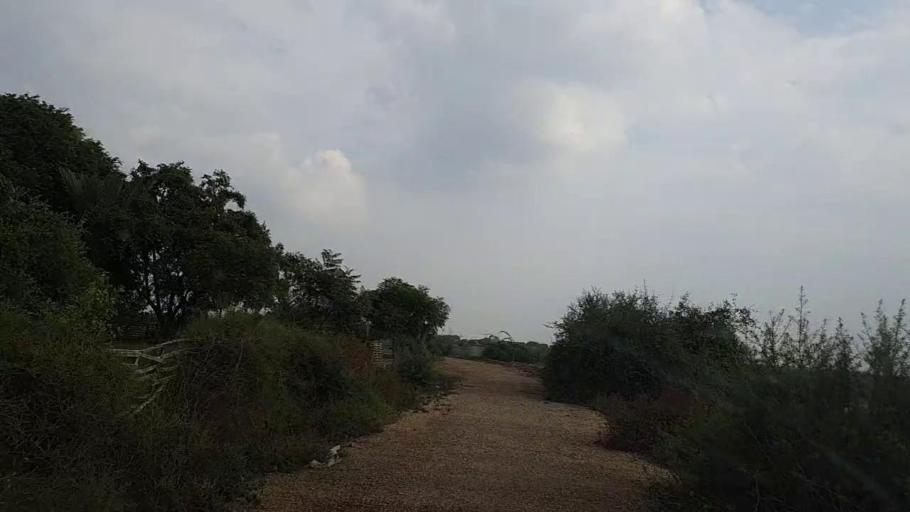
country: PK
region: Sindh
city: Daro Mehar
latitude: 24.6946
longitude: 68.1190
